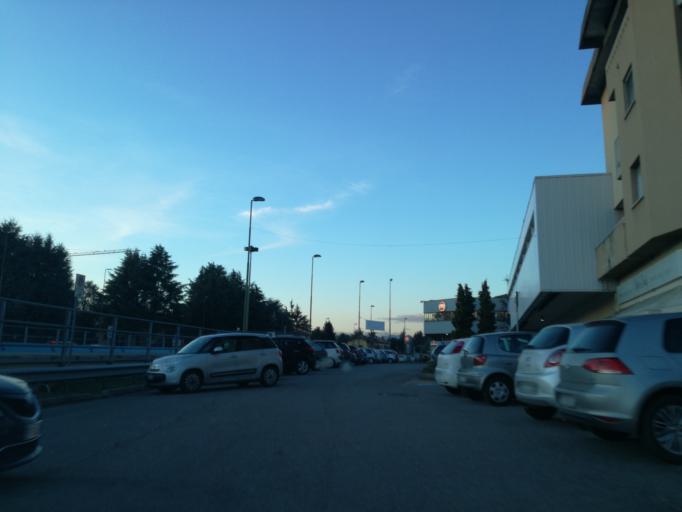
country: IT
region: Lombardy
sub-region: Provincia di Monza e Brianza
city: Vimercate
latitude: 45.6128
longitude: 9.3595
